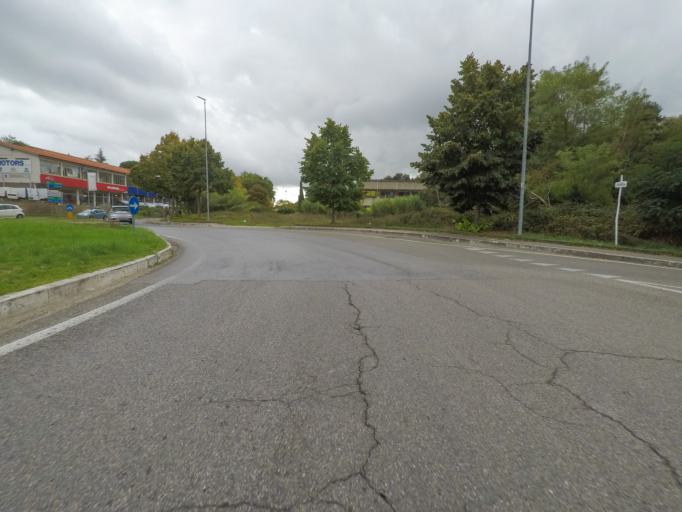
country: IT
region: Tuscany
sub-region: Provincia di Siena
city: Siena
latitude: 43.3211
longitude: 11.3499
